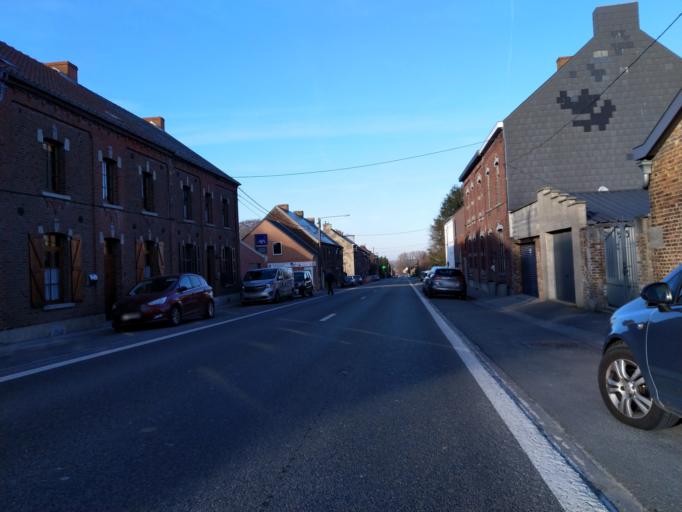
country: BE
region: Wallonia
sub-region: Province du Hainaut
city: Frameries
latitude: 50.3922
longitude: 3.9121
